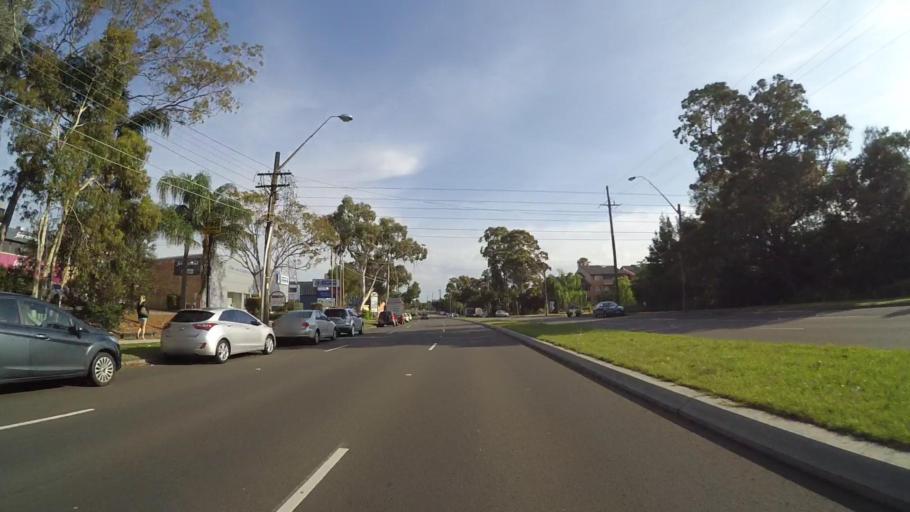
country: AU
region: New South Wales
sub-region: Sutherland Shire
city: Miranda
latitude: -34.0249
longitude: 151.1067
